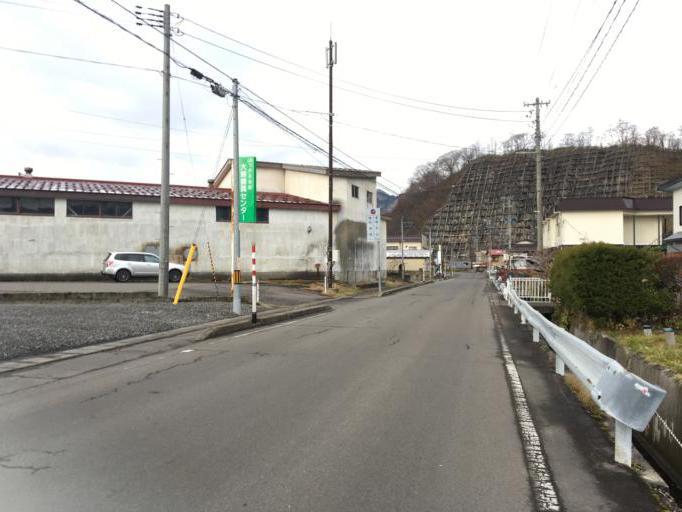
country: JP
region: Aomori
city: Hirosaki
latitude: 40.5227
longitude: 140.5655
